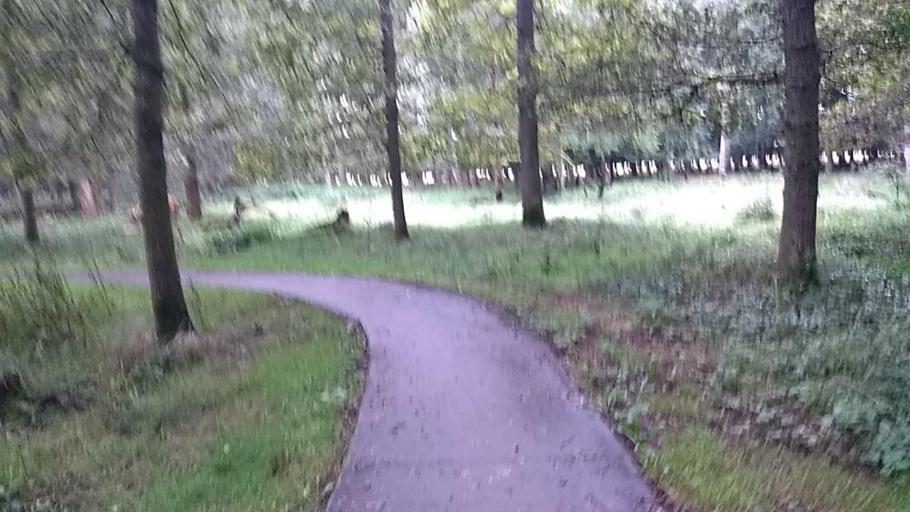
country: NL
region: Overijssel
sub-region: Gemeente Steenwijkerland
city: Vollenhove
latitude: 52.6663
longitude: 5.9356
